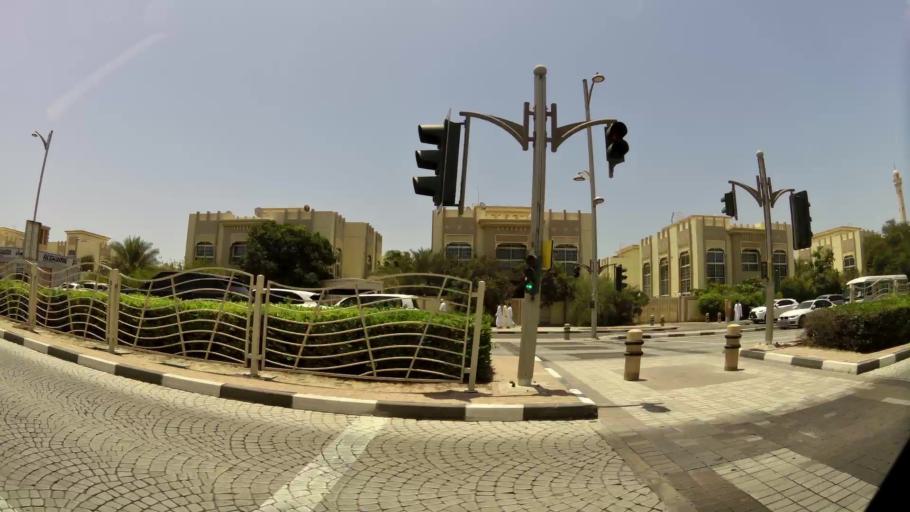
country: AE
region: Dubai
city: Dubai
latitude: 25.2126
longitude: 55.2486
